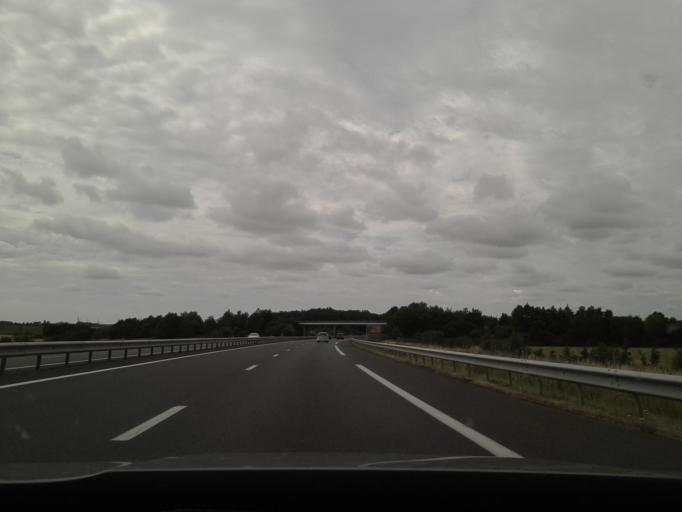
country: FR
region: Pays de la Loire
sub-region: Departement de la Sarthe
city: Saint-Paterne
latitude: 48.4264
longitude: 0.1381
